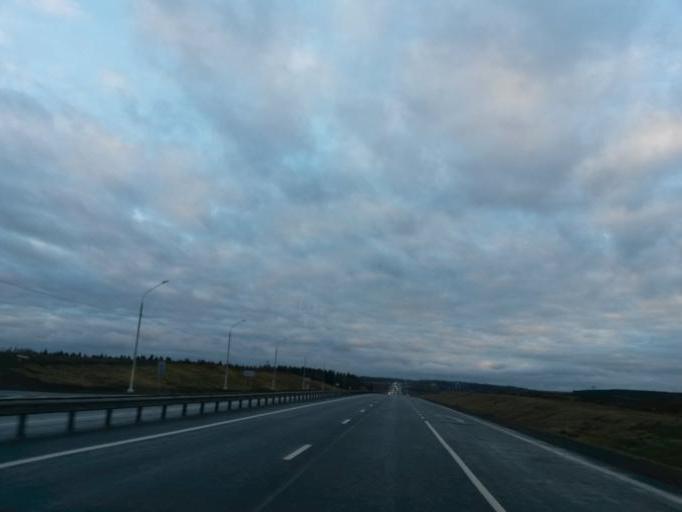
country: RU
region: Moskovskaya
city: Svatkovo
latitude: 56.3210
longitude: 38.2501
